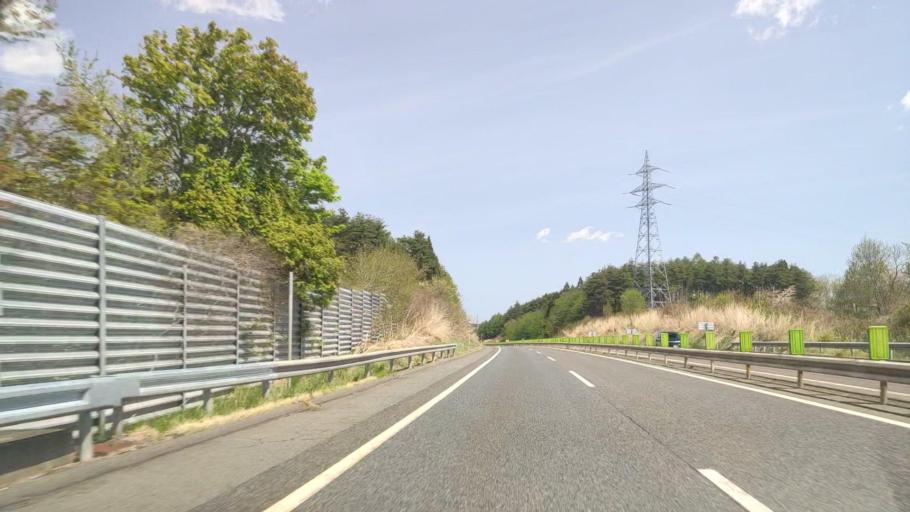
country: JP
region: Aomori
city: Hachinohe
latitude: 40.4345
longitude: 141.4452
